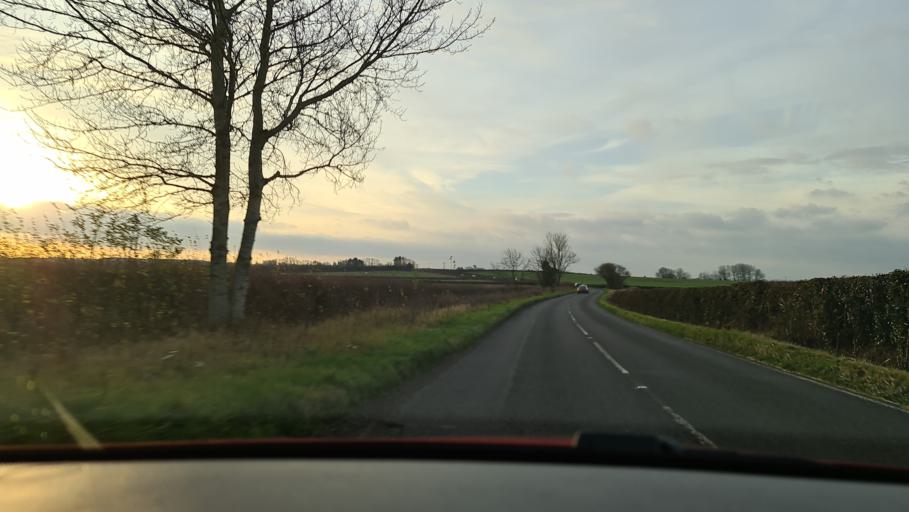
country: GB
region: England
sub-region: Oxfordshire
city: Kidlington
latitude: 51.8343
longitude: -1.2455
